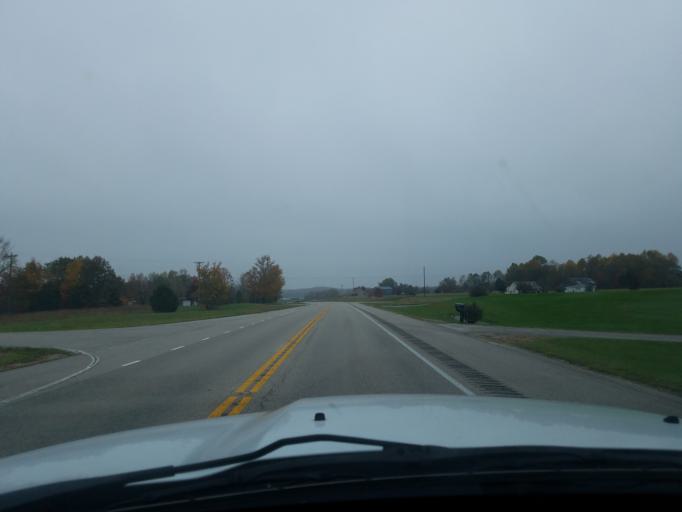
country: US
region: Kentucky
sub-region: Green County
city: Greensburg
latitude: 37.4156
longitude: -85.5004
